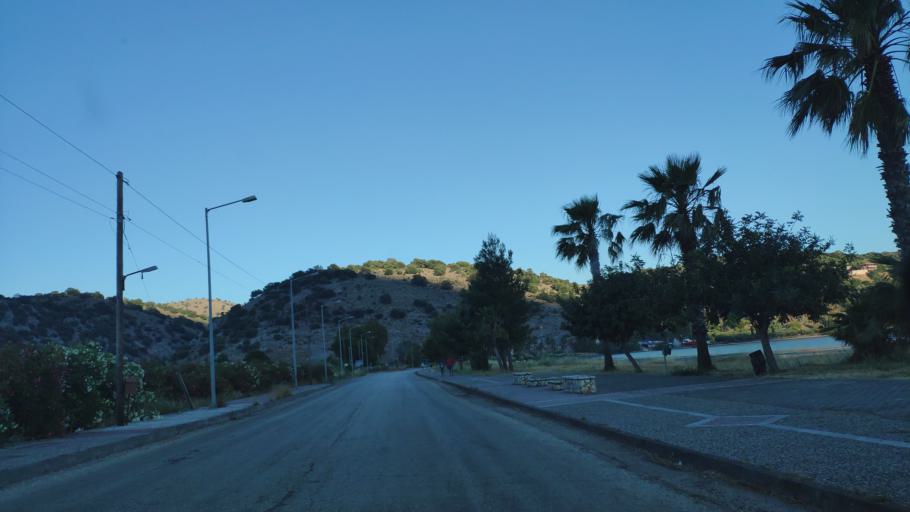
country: GR
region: West Greece
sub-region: Nomos Aitolias kai Akarnanias
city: Astakos
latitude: 38.5335
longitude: 21.0937
